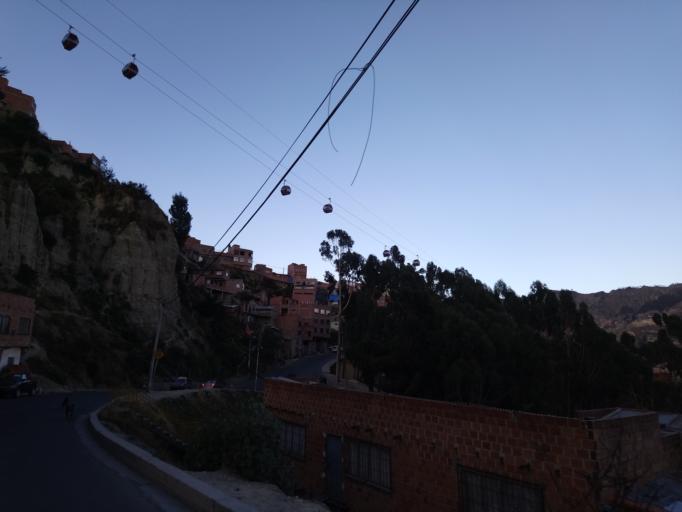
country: BO
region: La Paz
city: La Paz
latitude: -16.4867
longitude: -68.1279
